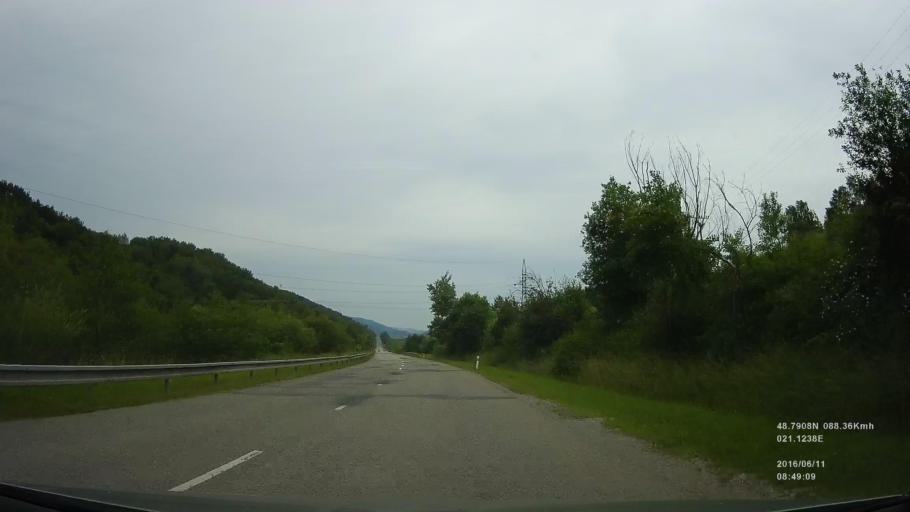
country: SK
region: Kosicky
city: Kosice
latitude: 48.7836
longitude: 21.1275
